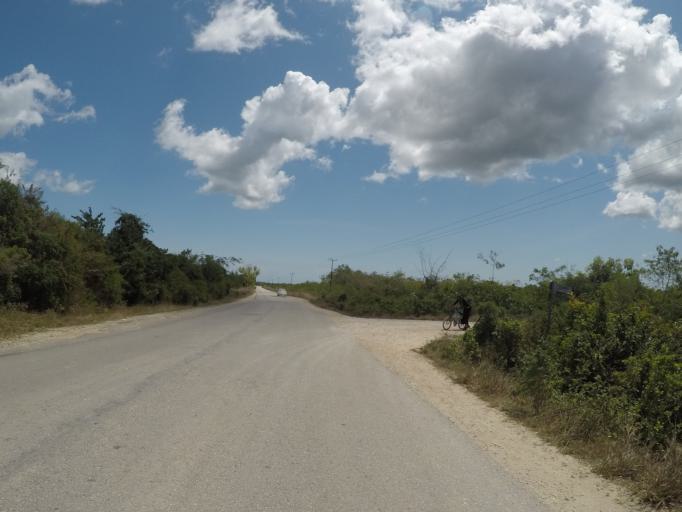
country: TZ
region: Zanzibar Central/South
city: Nganane
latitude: -6.2730
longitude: 39.4929
